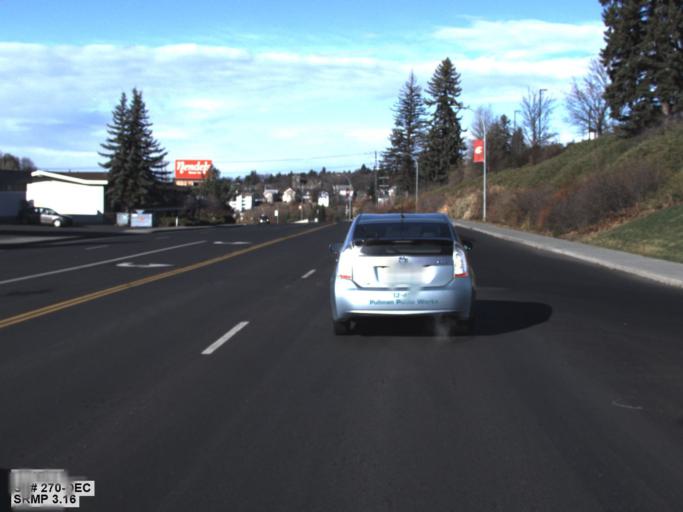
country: US
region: Washington
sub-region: Whitman County
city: Pullman
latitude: 46.7265
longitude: -117.1681
